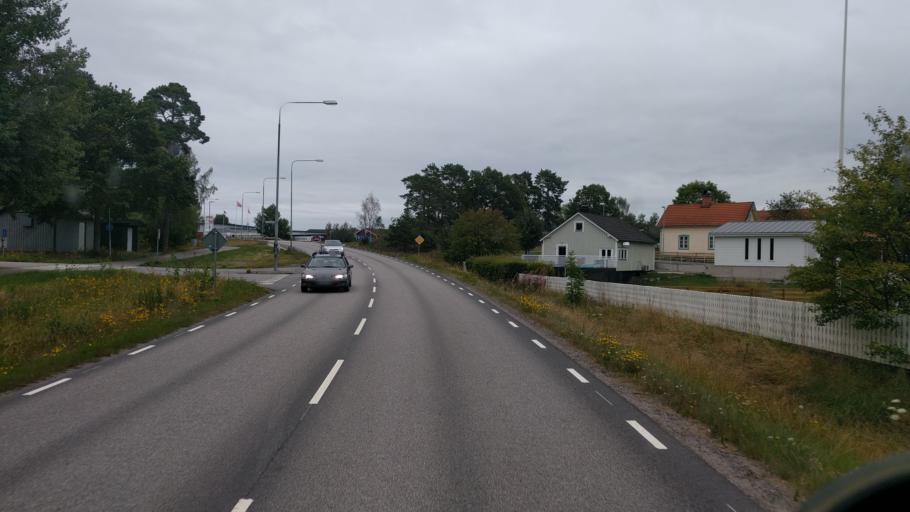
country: SE
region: Kalmar
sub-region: Vasterviks Kommun
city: Vaestervik
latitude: 57.7577
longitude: 16.6083
